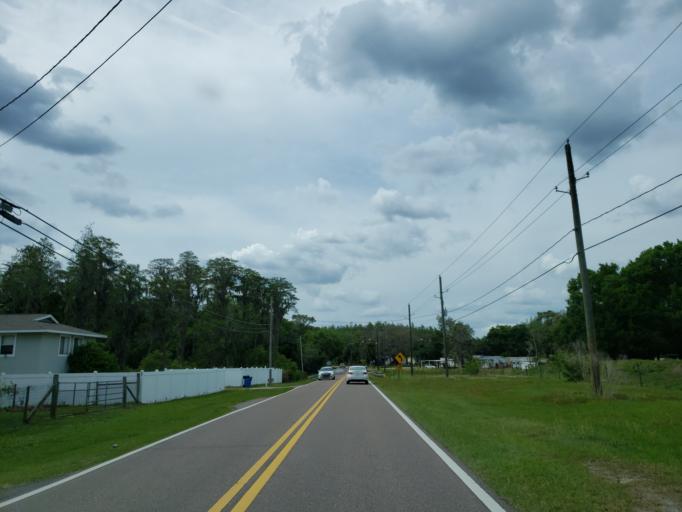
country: US
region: Florida
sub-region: Hillsborough County
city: Keystone
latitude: 28.1280
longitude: -82.6154
